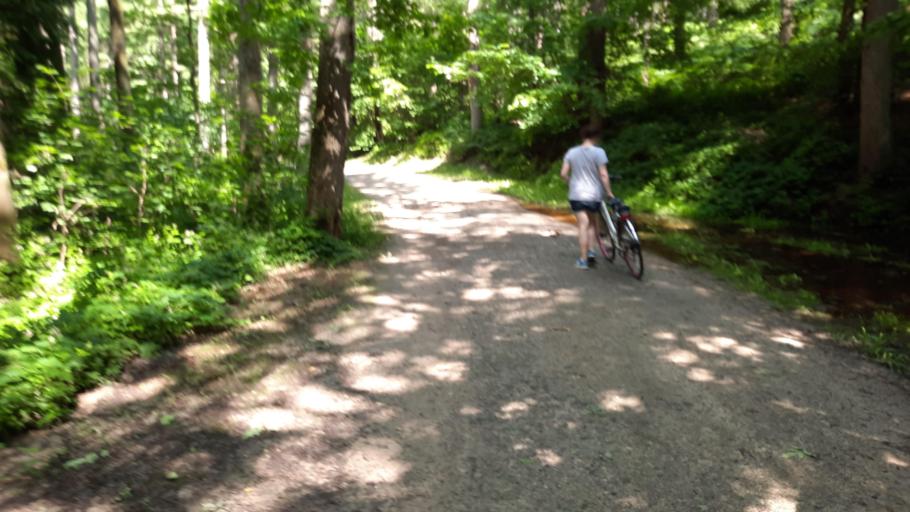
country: BE
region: Flanders
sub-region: Provincie Vlaams-Brabant
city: Tervuren
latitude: 50.8070
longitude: 4.5227
